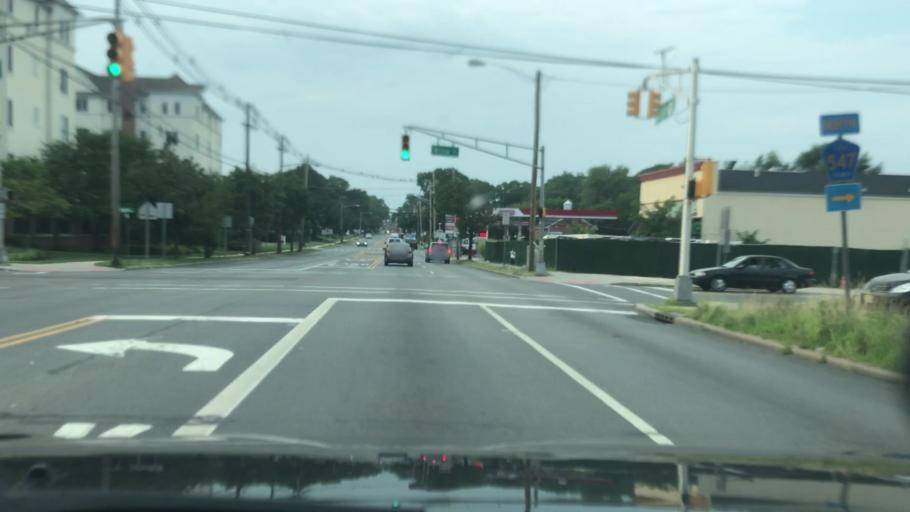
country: US
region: New Jersey
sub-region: Ocean County
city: Lakewood
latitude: 40.0986
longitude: -74.2179
